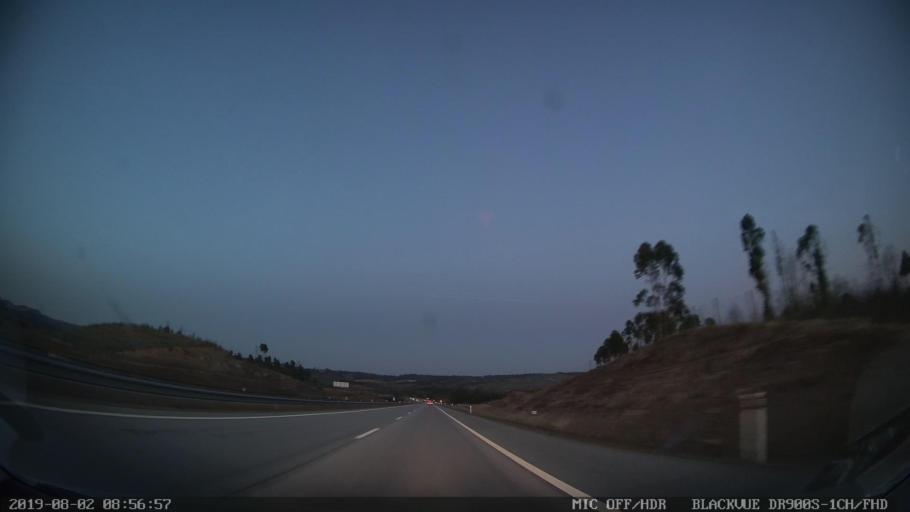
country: PT
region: Portalegre
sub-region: Gaviao
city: Gaviao
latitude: 39.5343
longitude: -7.9131
